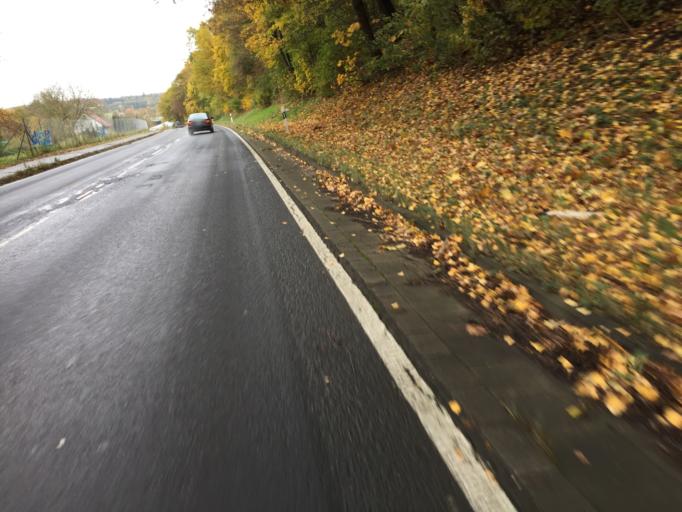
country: DE
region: Hesse
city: Staufenberg
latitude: 50.6585
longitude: 8.7159
